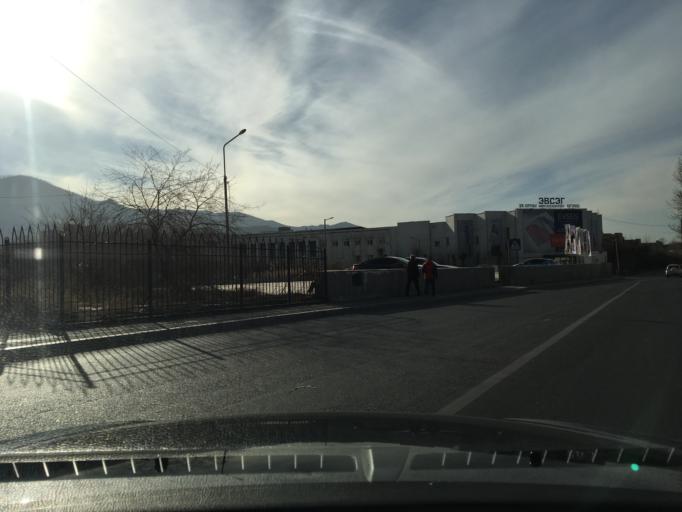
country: MN
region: Ulaanbaatar
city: Ulaanbaatar
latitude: 47.8962
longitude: 106.9073
